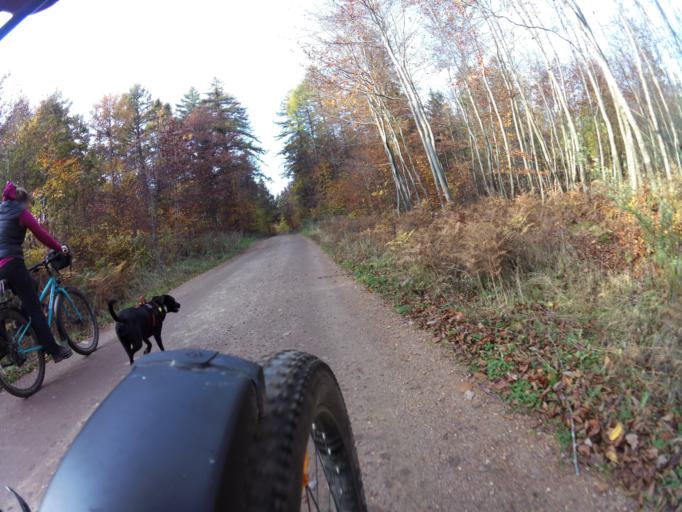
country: PL
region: Pomeranian Voivodeship
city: Strzelno
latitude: 54.7399
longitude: 18.2600
